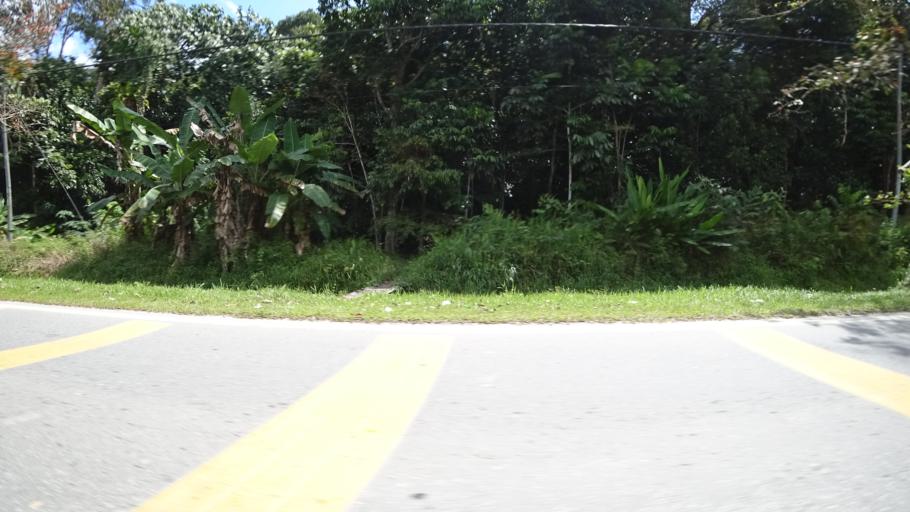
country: MY
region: Sarawak
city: Limbang
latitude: 4.6915
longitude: 114.9823
